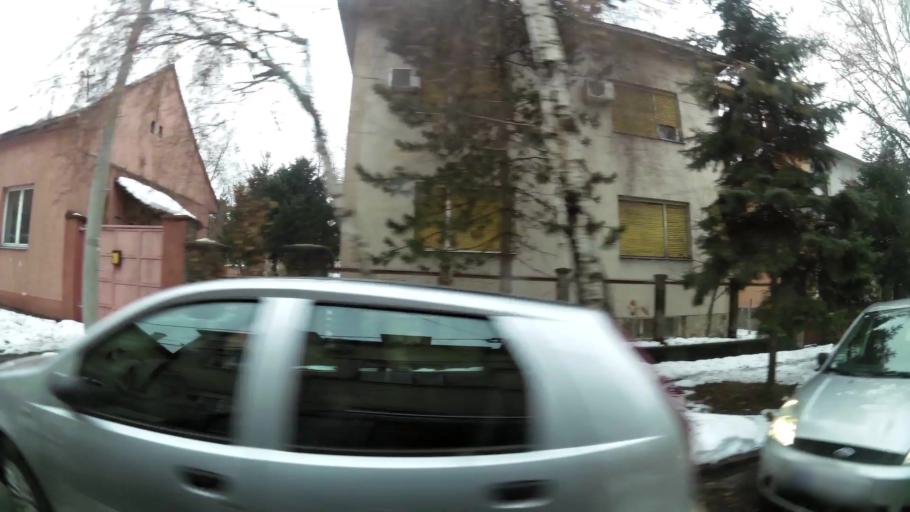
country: RS
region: Central Serbia
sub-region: Belgrade
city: Zemun
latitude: 44.8461
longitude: 20.4032
